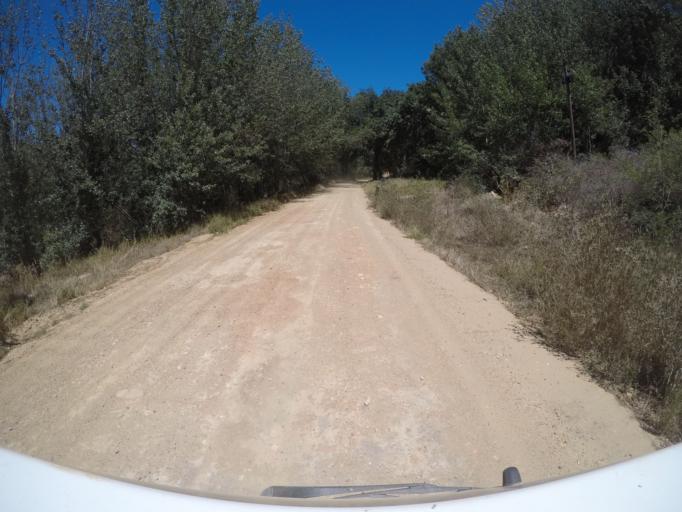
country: ZA
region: Western Cape
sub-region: Overberg District Municipality
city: Caledon
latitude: -34.1564
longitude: 19.2306
